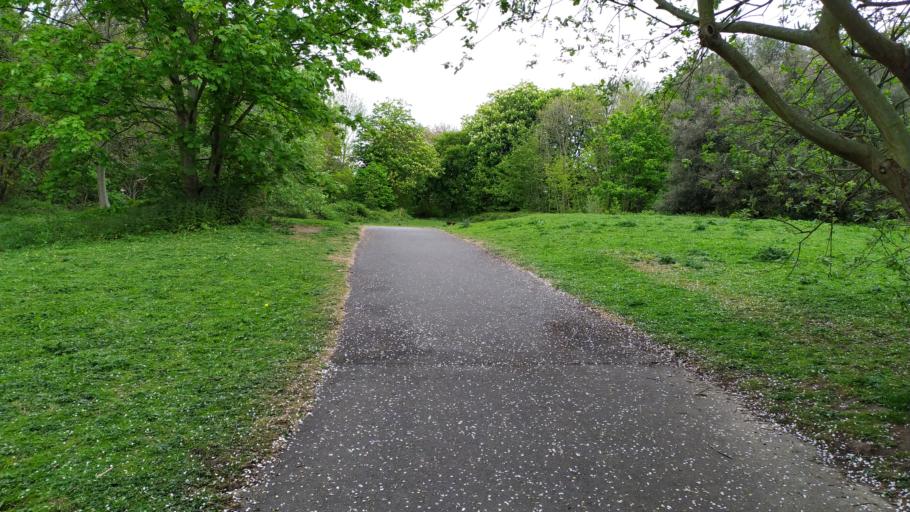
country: GB
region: England
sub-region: City and Borough of Leeds
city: Shadwell
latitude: 53.8064
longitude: -1.4818
